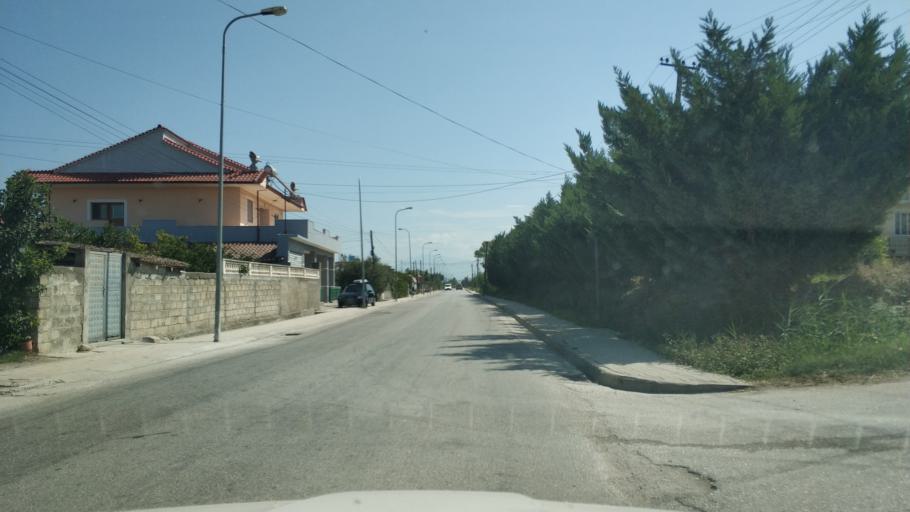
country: AL
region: Fier
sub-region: Rrethi i Lushnjes
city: Gradishte
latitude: 40.8930
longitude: 19.6344
